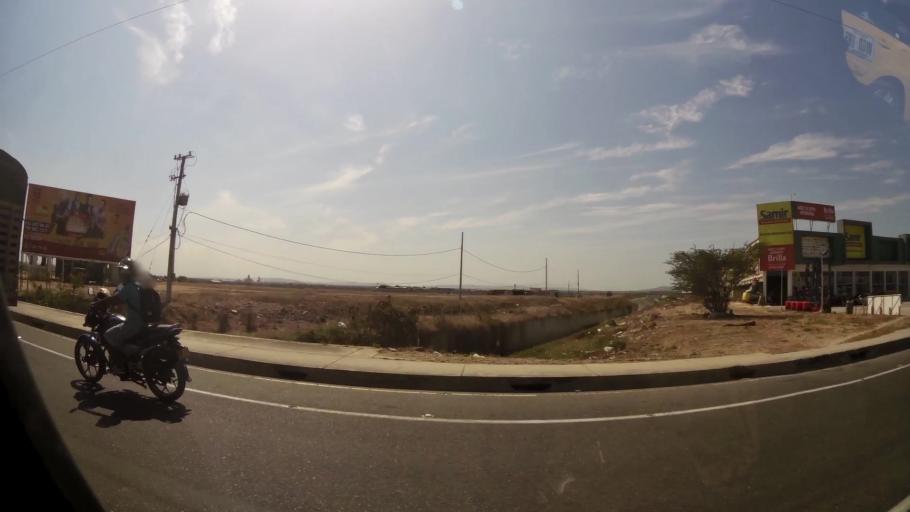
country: CO
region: Atlantico
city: Barranquilla
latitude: 10.9542
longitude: -74.8359
